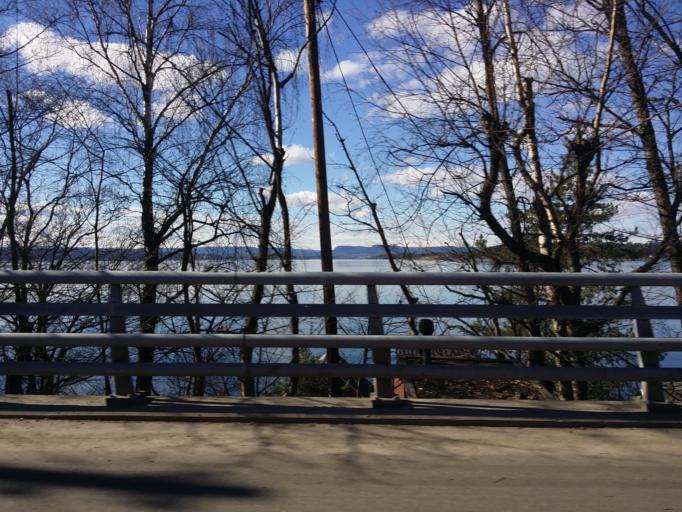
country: NO
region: Akershus
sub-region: Oppegard
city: Kolbotn
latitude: 59.8497
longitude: 10.7812
